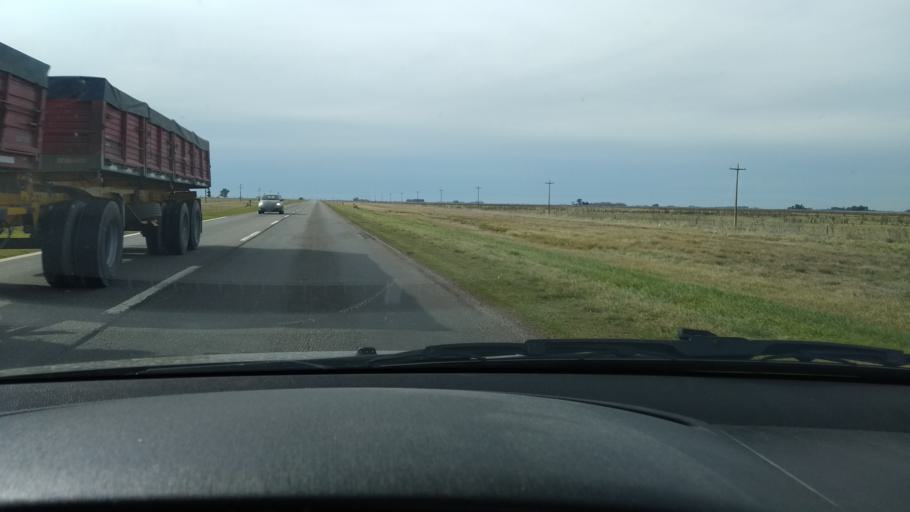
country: AR
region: Buenos Aires
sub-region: Partido de Azul
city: Azul
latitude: -36.6844
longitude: -59.7310
